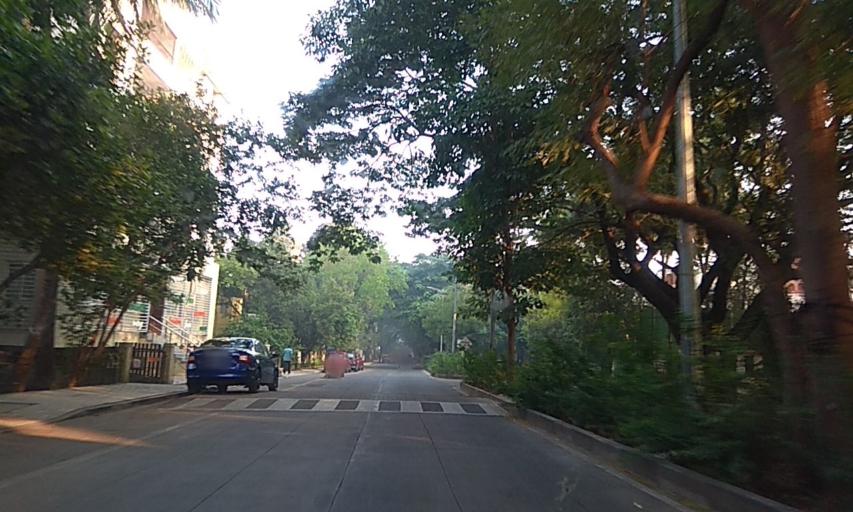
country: IN
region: Maharashtra
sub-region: Pune Division
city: Shivaji Nagar
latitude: 18.5433
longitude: 73.8173
